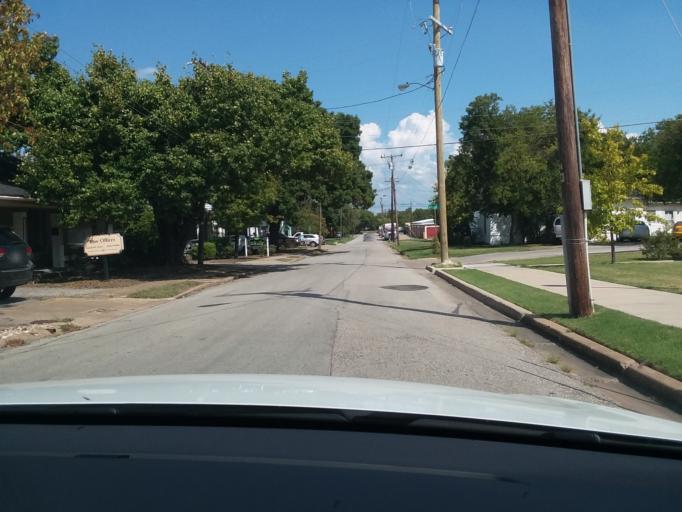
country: US
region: Texas
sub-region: Collin County
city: McKinney
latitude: 33.2006
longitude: -96.6146
